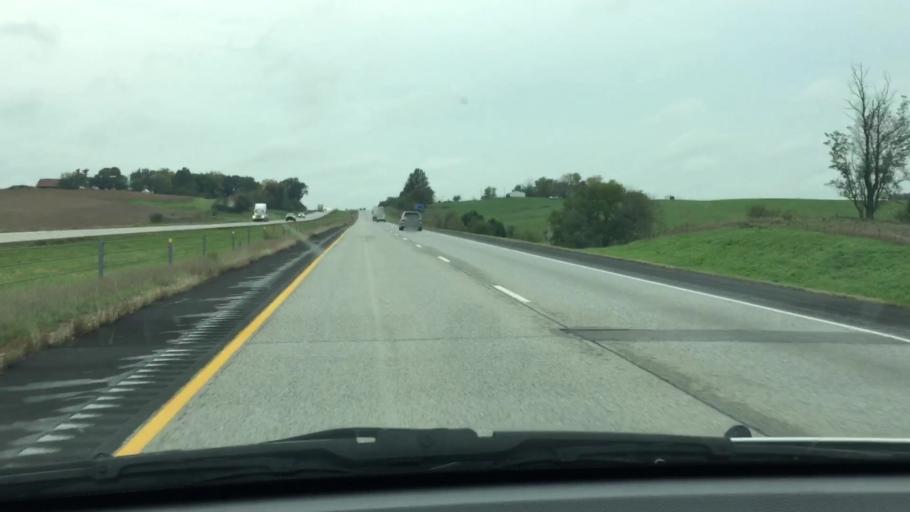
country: US
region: Iowa
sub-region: Johnson County
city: Tiffin
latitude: 41.6952
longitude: -91.7096
